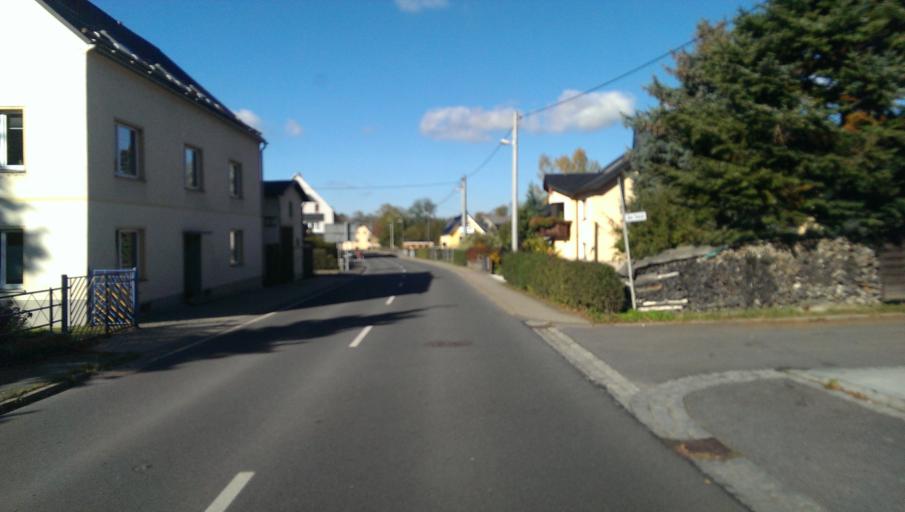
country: DE
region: Saxony
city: Eppendorf
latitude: 50.7851
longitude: 13.2678
